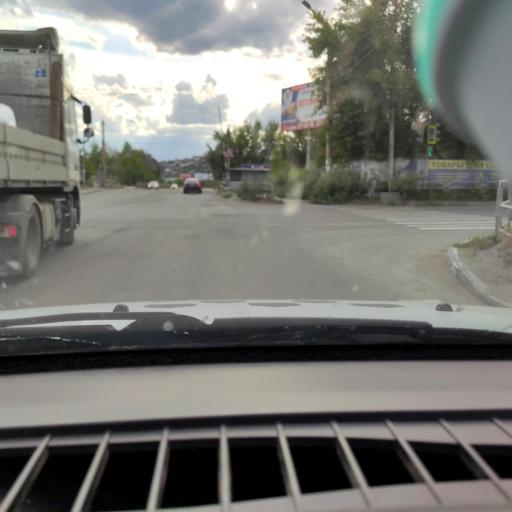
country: RU
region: Chelyabinsk
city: Miass
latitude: 55.0647
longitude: 60.1042
